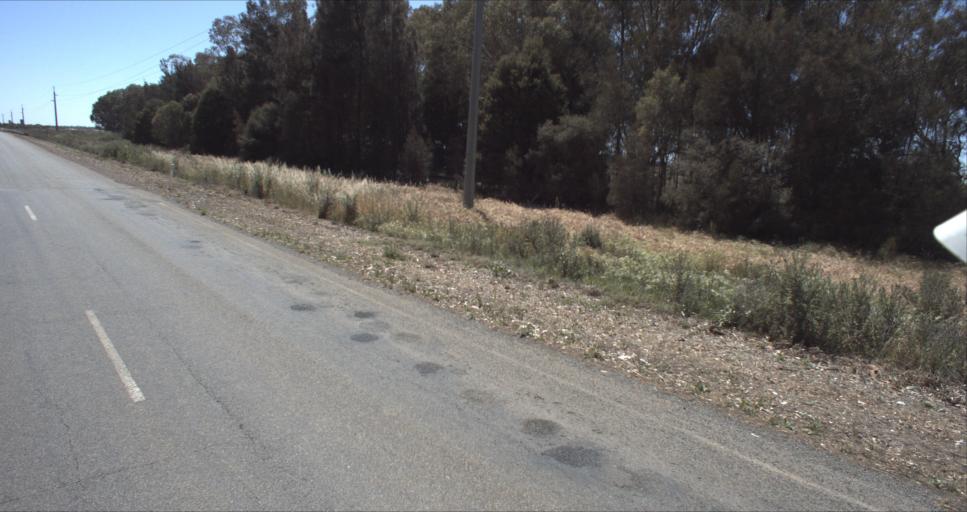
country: AU
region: New South Wales
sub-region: Leeton
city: Leeton
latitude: -34.4662
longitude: 146.2932
